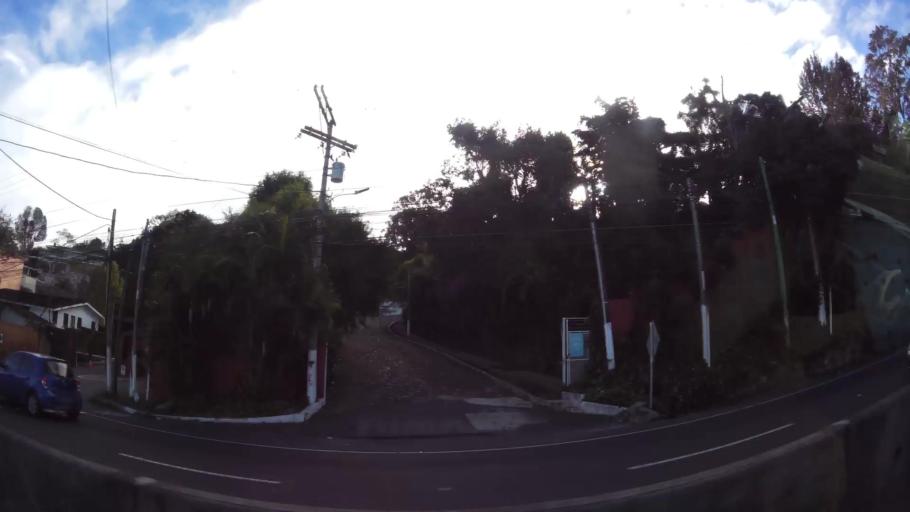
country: GT
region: Guatemala
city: Santa Catarina Pinula
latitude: 14.5782
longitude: -90.4824
